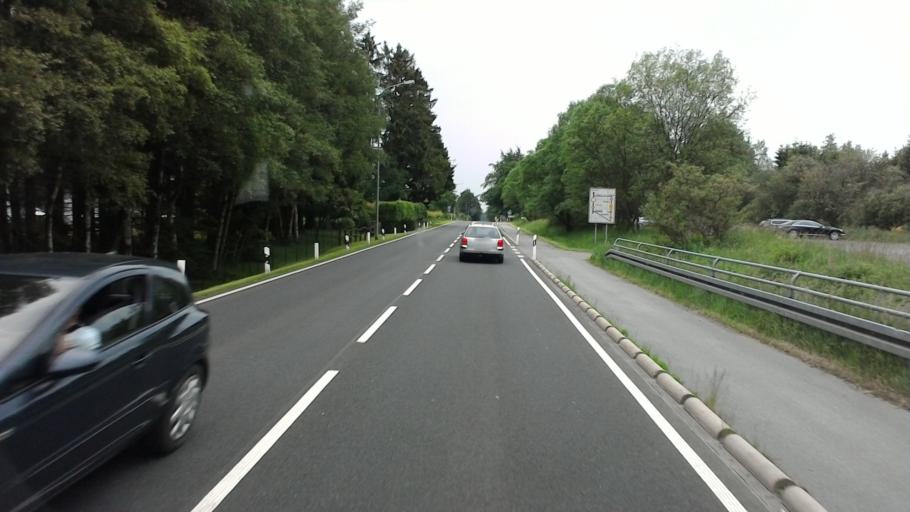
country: DE
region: North Rhine-Westphalia
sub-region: Regierungsbezirk Koln
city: Monschau
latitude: 50.6013
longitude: 6.2483
